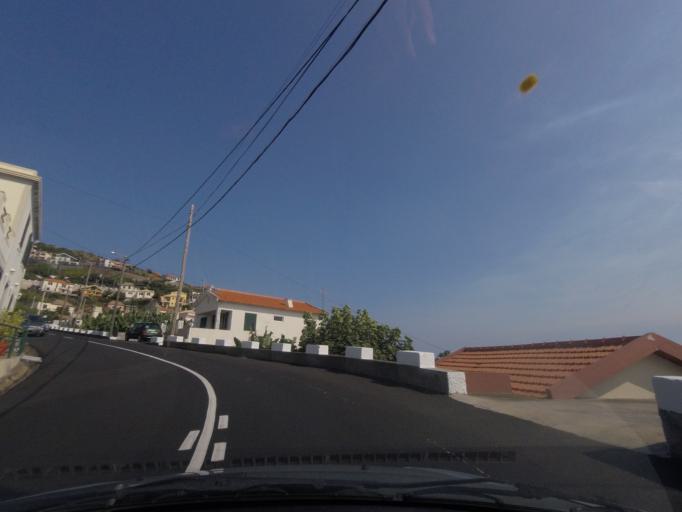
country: PT
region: Madeira
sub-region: Ribeira Brava
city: Campanario
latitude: 32.6678
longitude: -17.0525
